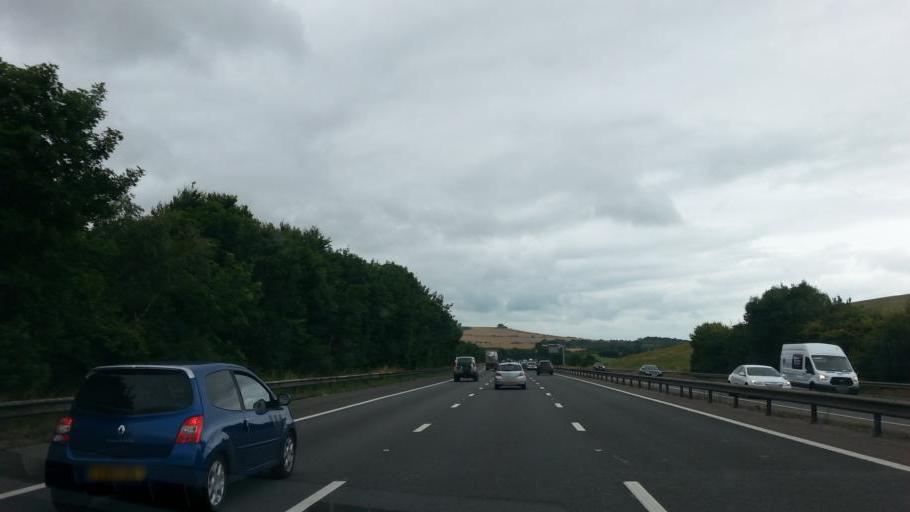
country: GB
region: England
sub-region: Borough of Swindon
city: Bishopstone
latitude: 51.5141
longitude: -1.6378
